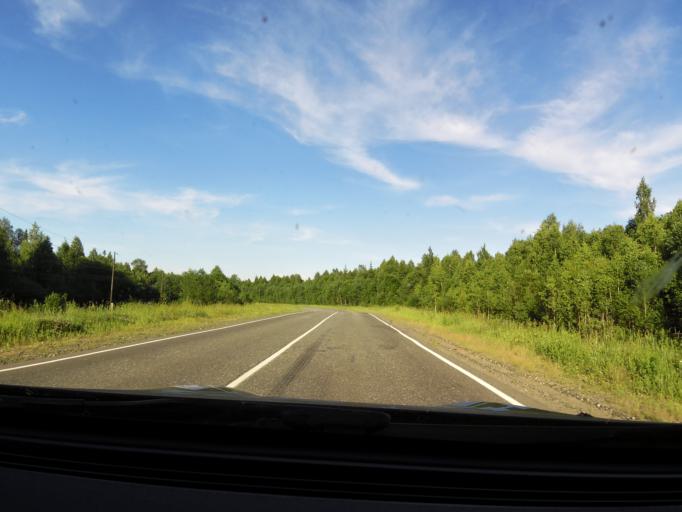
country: RU
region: Kirov
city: Lesnyye Polyany
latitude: 58.8018
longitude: 52.5797
